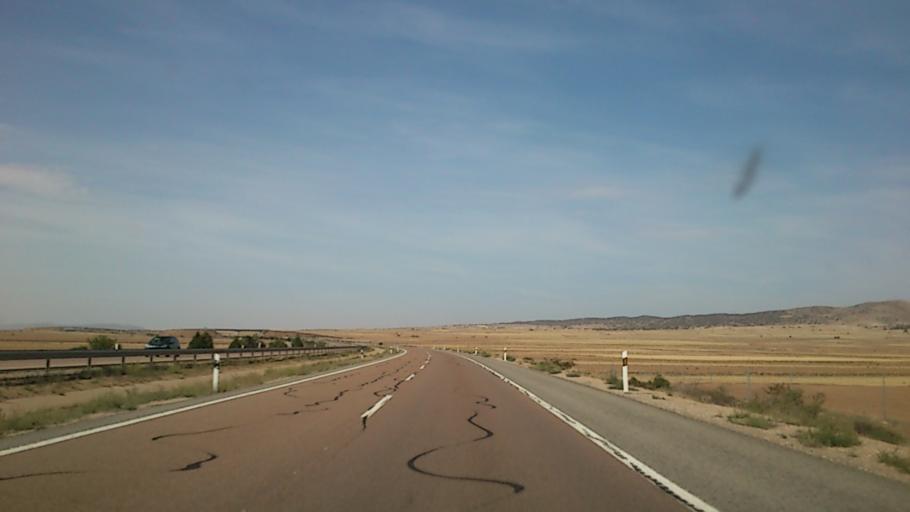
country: ES
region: Aragon
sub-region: Provincia de Teruel
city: Singra
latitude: 40.6686
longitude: -1.3145
